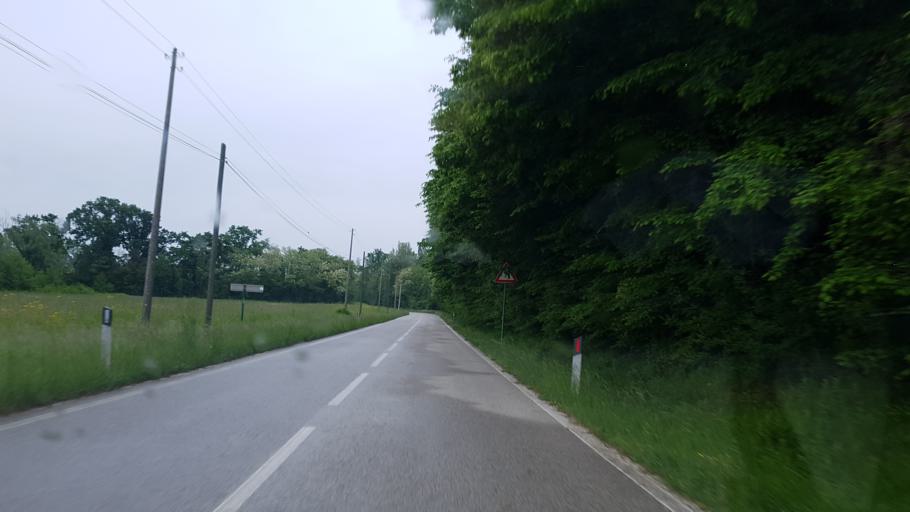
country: IT
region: Friuli Venezia Giulia
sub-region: Provincia di Udine
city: Corno di Rosazzo
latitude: 45.9894
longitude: 13.4209
